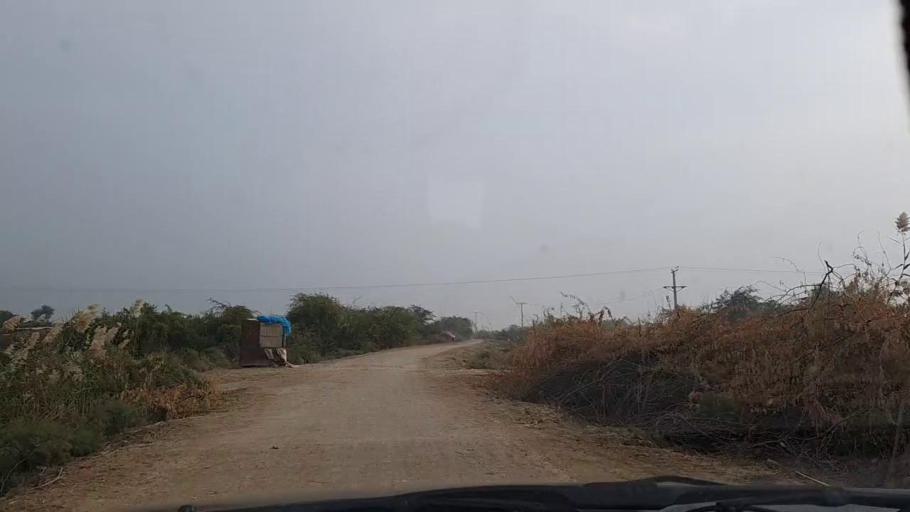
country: PK
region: Sindh
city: Tando Mittha Khan
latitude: 25.8049
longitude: 69.3788
